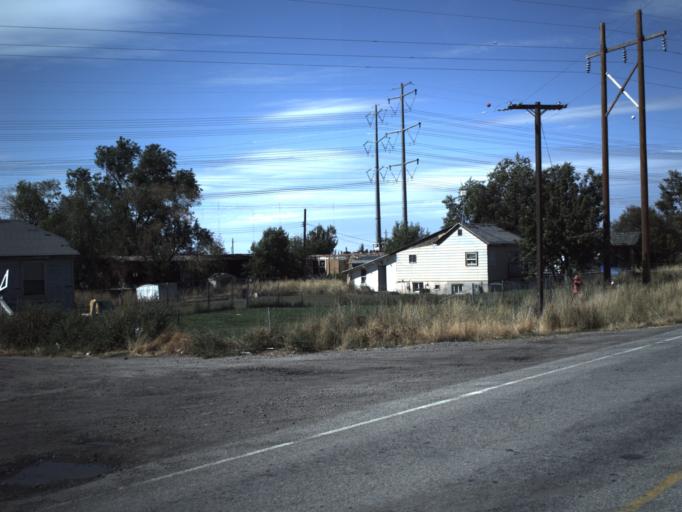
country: US
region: Utah
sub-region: Davis County
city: West Bountiful
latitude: 40.8812
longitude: -111.9300
